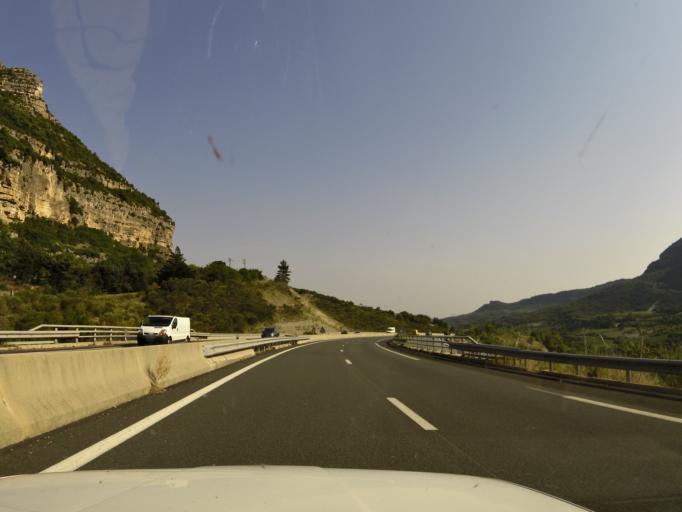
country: FR
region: Languedoc-Roussillon
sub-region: Departement de l'Herault
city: Lodeve
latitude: 43.7959
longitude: 3.3263
